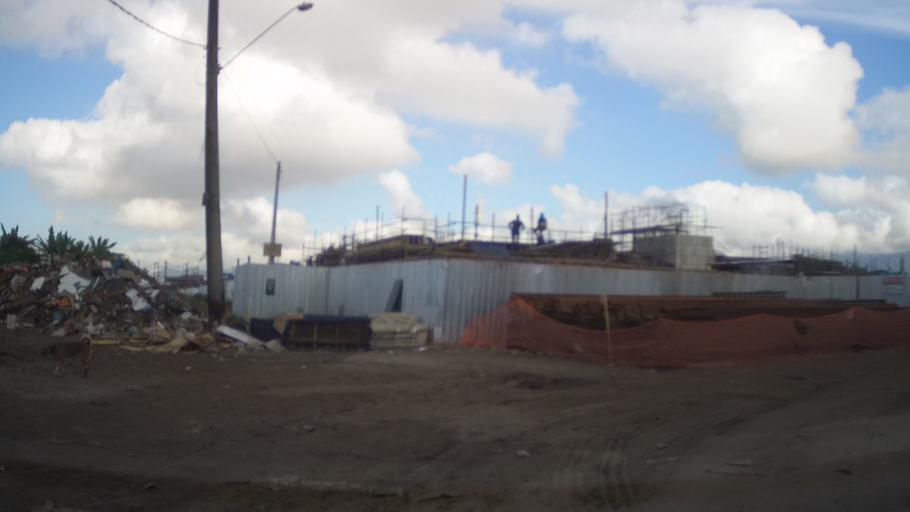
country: BR
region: Sao Paulo
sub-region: Praia Grande
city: Praia Grande
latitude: -24.0122
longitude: -46.4734
